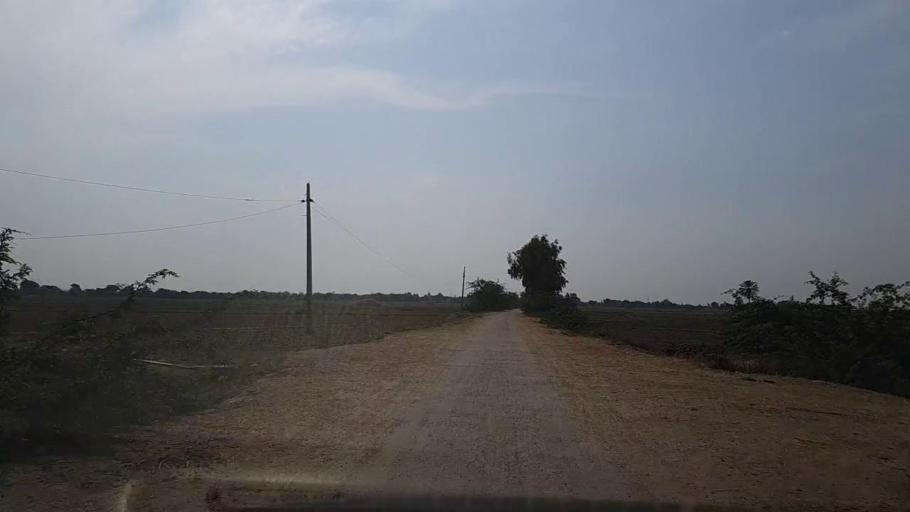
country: PK
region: Sindh
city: Thatta
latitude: 24.7972
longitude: 67.8754
